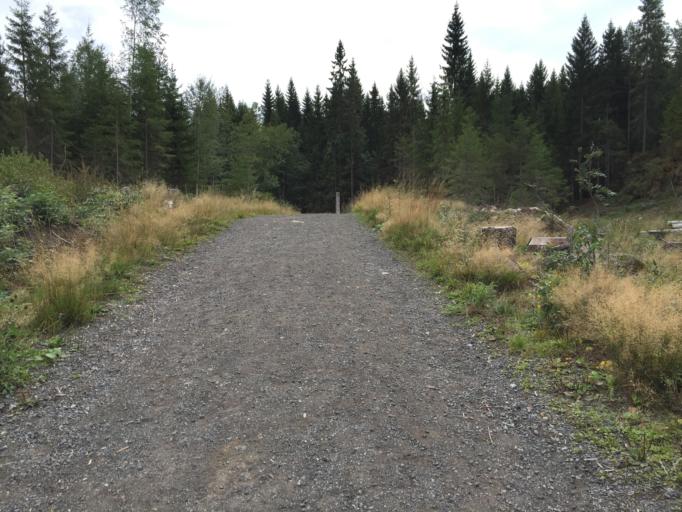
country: NO
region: Akershus
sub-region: Raelingen
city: Fjerdingby
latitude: 59.9175
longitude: 11.0140
